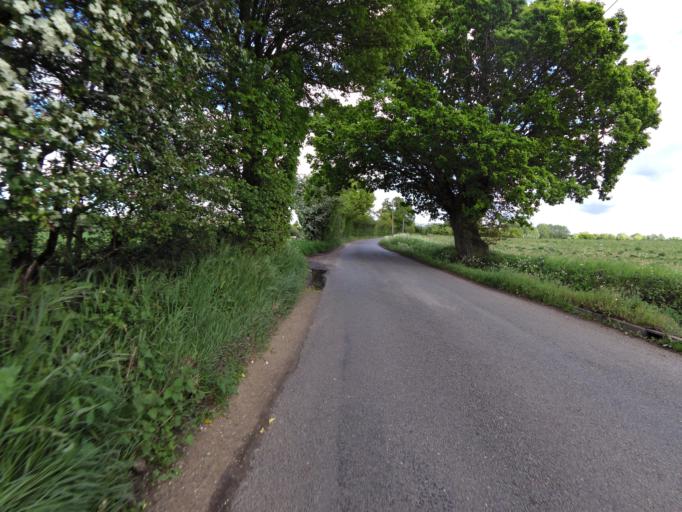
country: GB
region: England
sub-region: Suffolk
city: Woolpit
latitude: 52.2217
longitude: 0.8762
